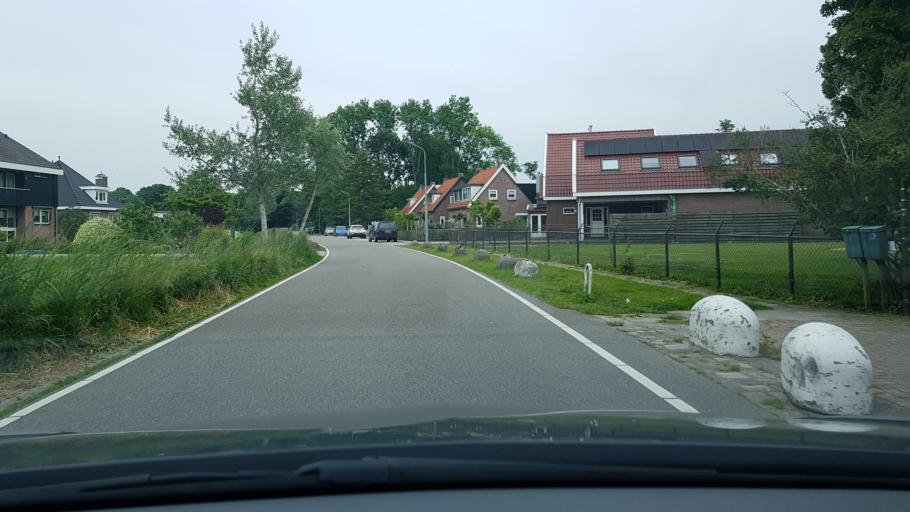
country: NL
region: North Holland
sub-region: Gemeente Haarlemmermeer
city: Hoofddorp
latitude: 52.3537
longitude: 4.7546
